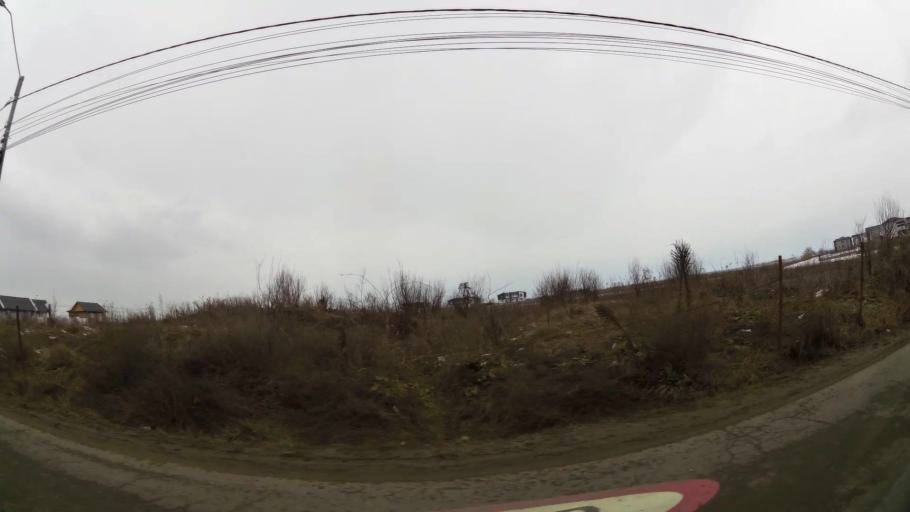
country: RO
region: Ilfov
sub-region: Comuna Otopeni
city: Otopeni
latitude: 44.5527
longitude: 26.1075
